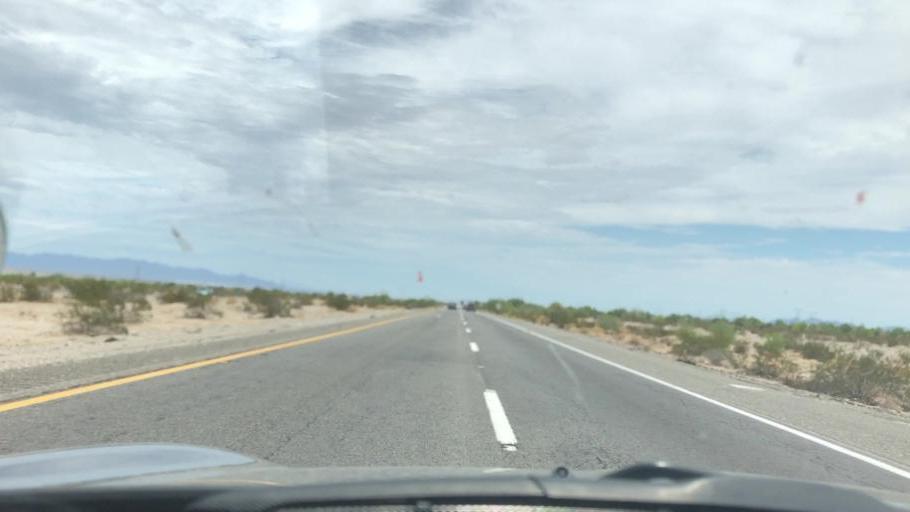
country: US
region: California
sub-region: Riverside County
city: Mesa Verde
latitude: 33.6798
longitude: -115.2356
